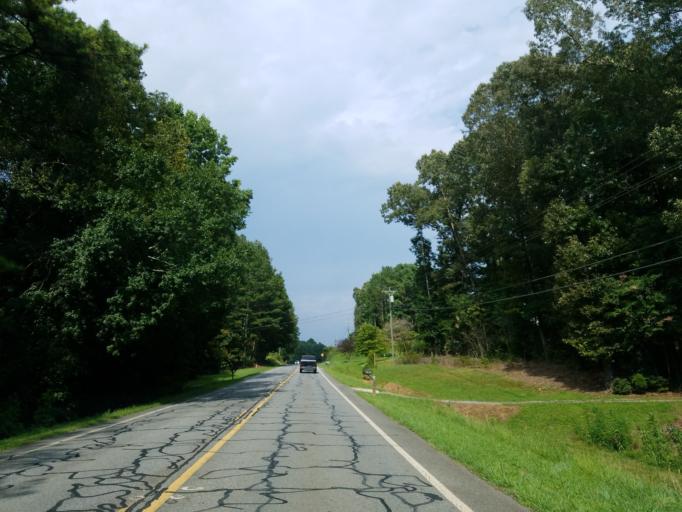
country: US
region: Georgia
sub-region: Gilmer County
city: Ellijay
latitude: 34.6421
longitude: -84.5587
